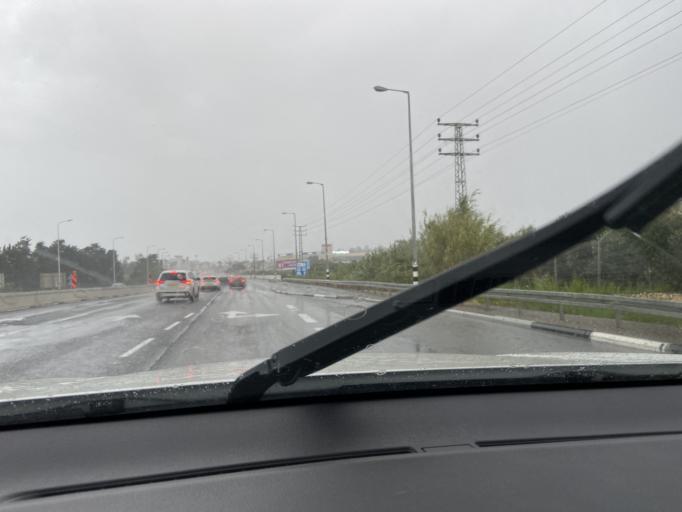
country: IL
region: Northern District
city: El Mazra`a
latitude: 32.9832
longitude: 35.0949
